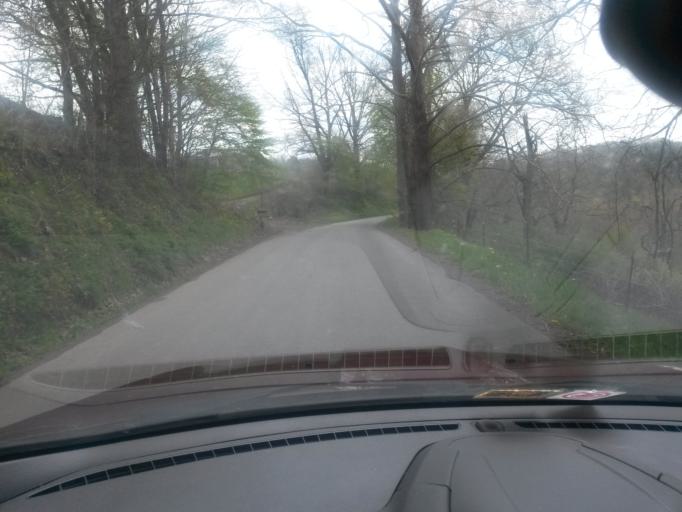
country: US
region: West Virginia
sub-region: Greenbrier County
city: White Sulphur Springs
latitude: 38.0397
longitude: -80.3421
